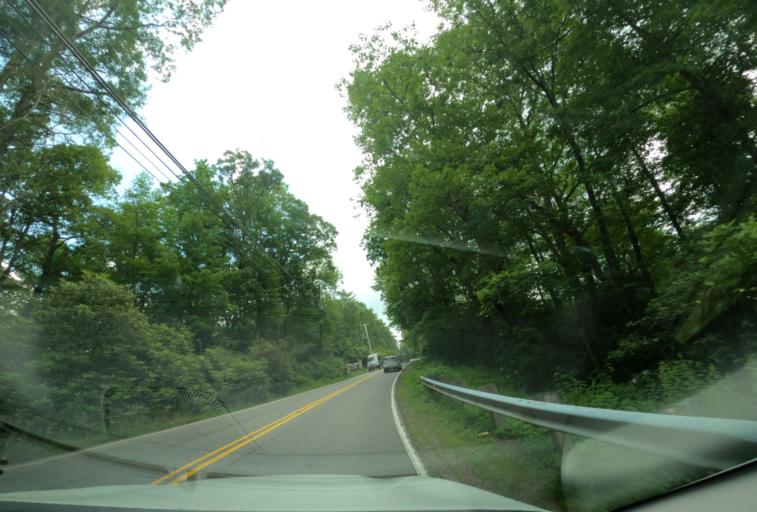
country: US
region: North Carolina
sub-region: Jackson County
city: Cullowhee
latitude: 35.0886
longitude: -83.1629
